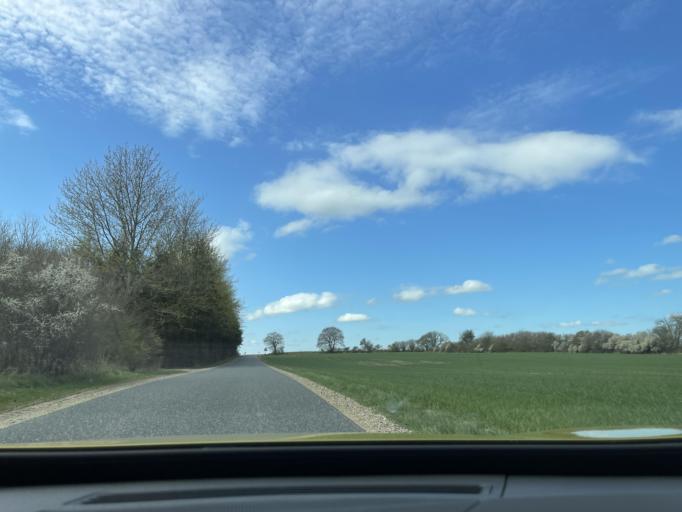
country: DK
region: Central Jutland
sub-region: Favrskov Kommune
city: Hinnerup
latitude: 56.2796
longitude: 10.0585
